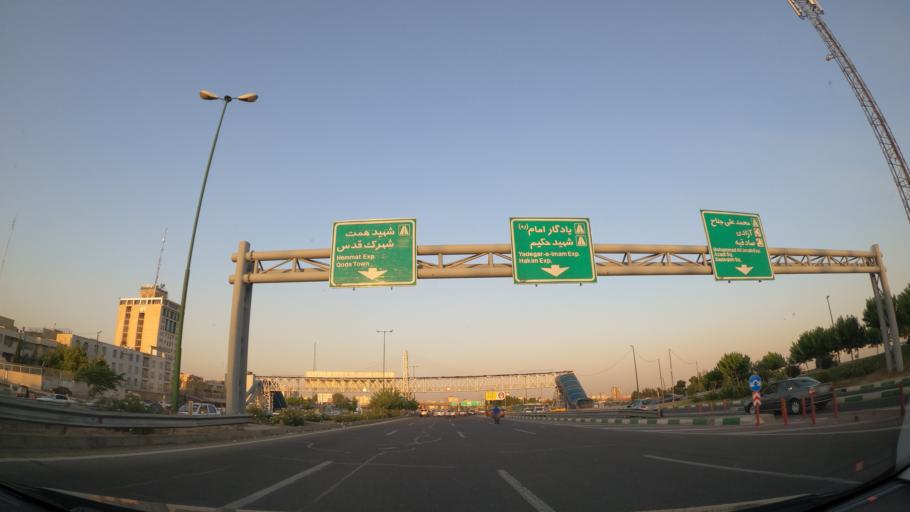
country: IR
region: Tehran
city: Tehran
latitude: 35.7134
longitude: 51.3302
